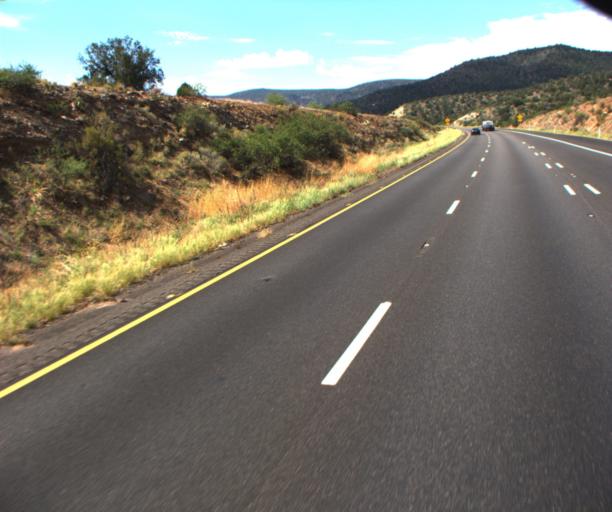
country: US
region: Arizona
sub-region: Yavapai County
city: Camp Verde
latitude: 34.5589
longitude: -111.9072
